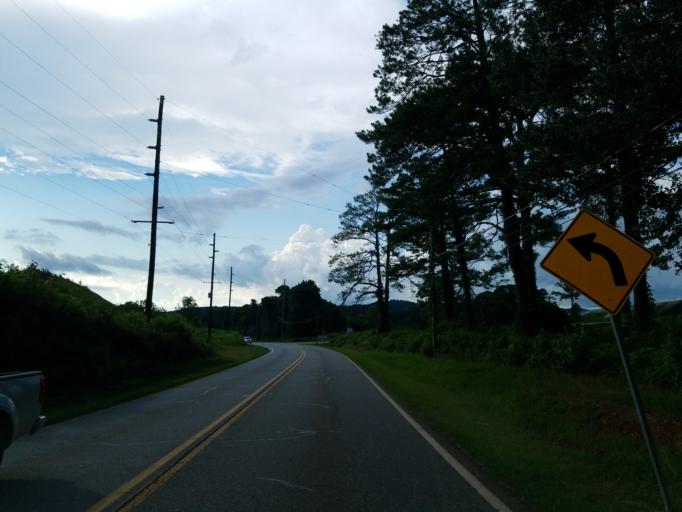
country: US
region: Georgia
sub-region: Bartow County
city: Emerson
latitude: 34.1416
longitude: -84.7652
